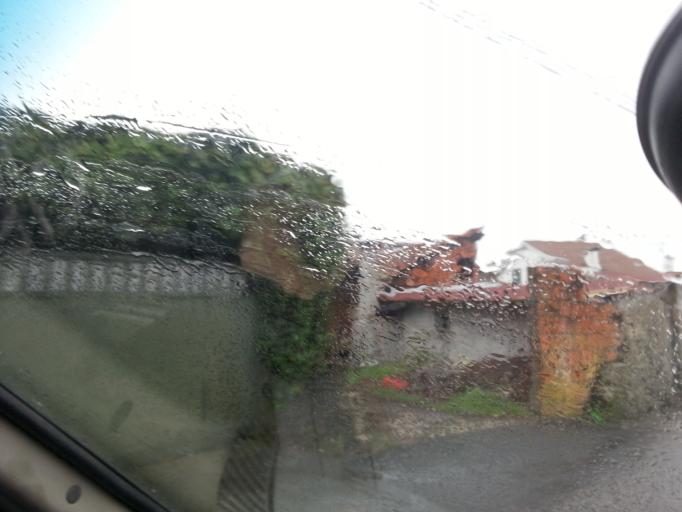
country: PT
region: Viseu
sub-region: Viseu
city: Rio de Loba
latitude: 40.6626
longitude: -7.8765
